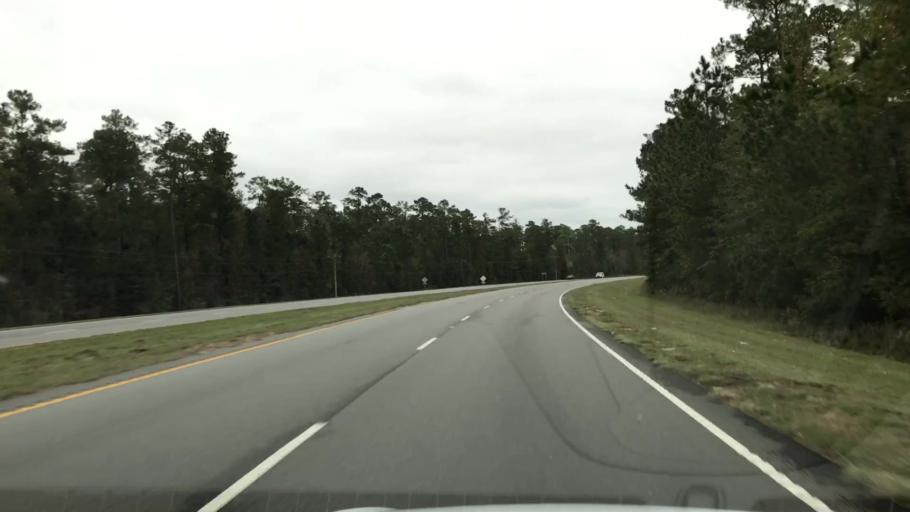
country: US
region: South Carolina
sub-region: Georgetown County
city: Georgetown
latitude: 33.2514
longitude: -79.3745
